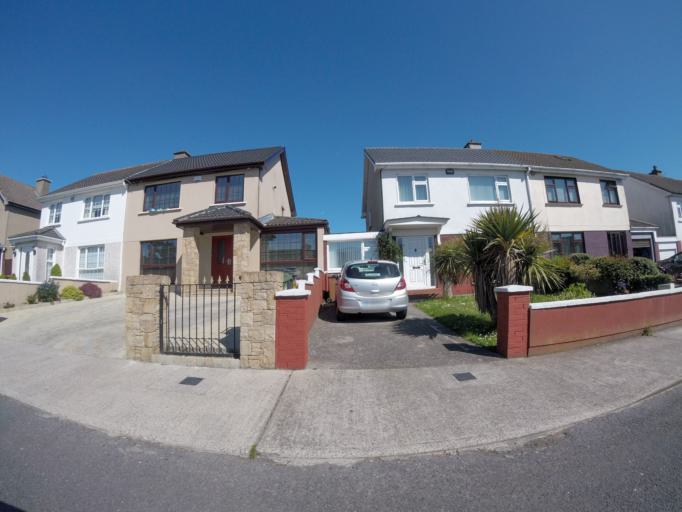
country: IE
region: Munster
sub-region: Waterford
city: Waterford
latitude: 52.2531
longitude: -7.1445
